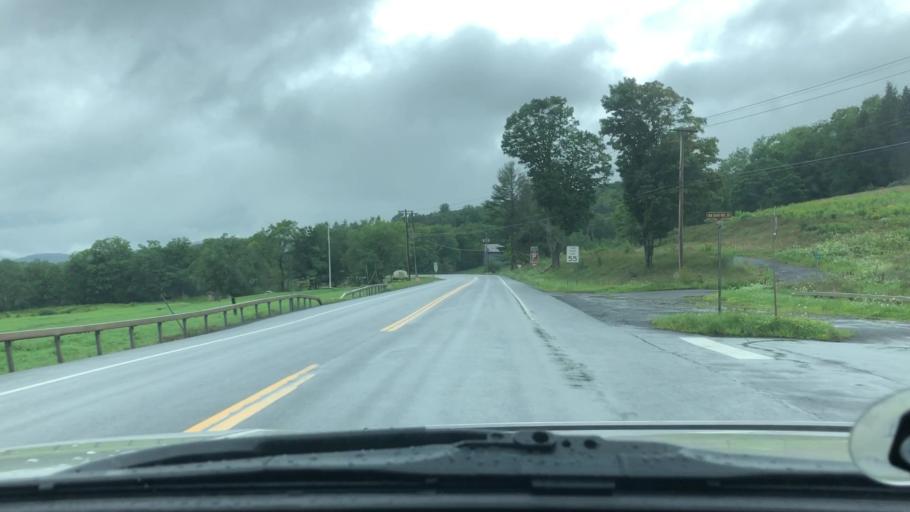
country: US
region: New York
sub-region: Greene County
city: Cairo
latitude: 42.3046
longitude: -74.2175
